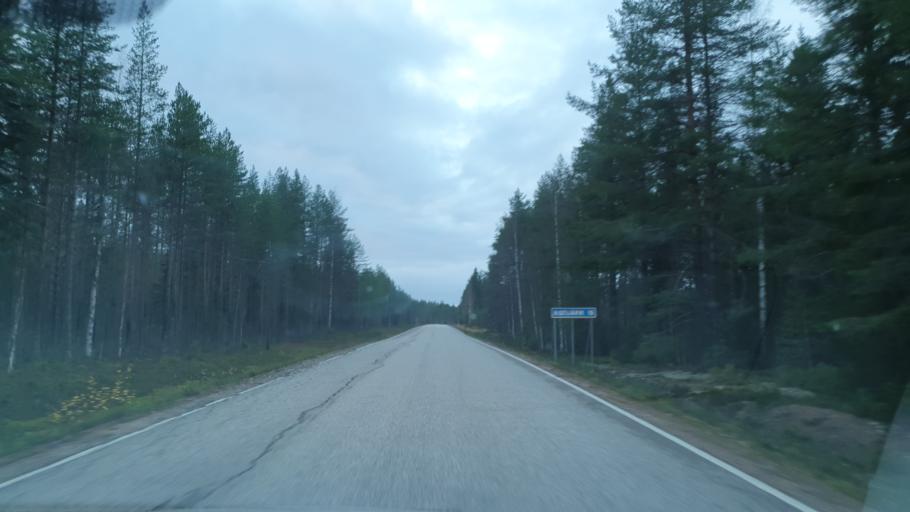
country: FI
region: Kainuu
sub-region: Kajaani
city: Ristijaervi
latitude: 64.4208
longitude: 28.4084
